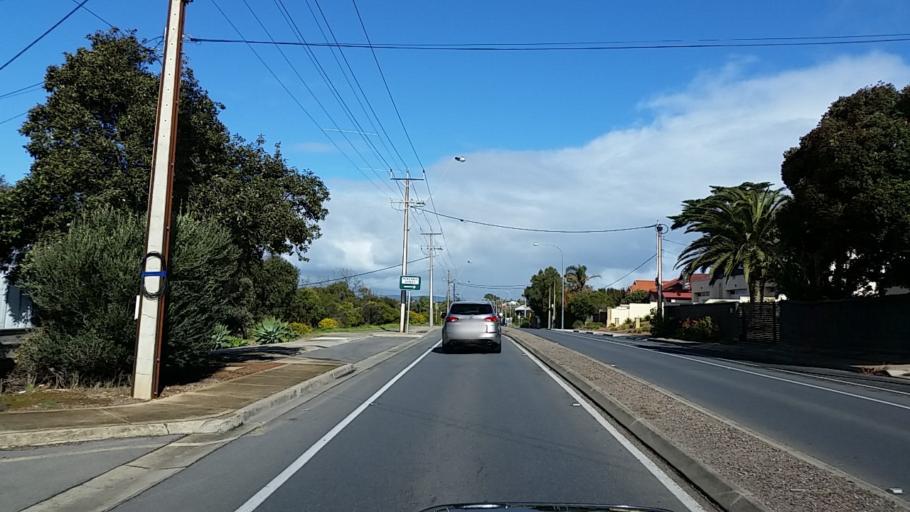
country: AU
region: South Australia
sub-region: Adelaide
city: Port Noarlunga
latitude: -35.1575
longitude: 138.4749
